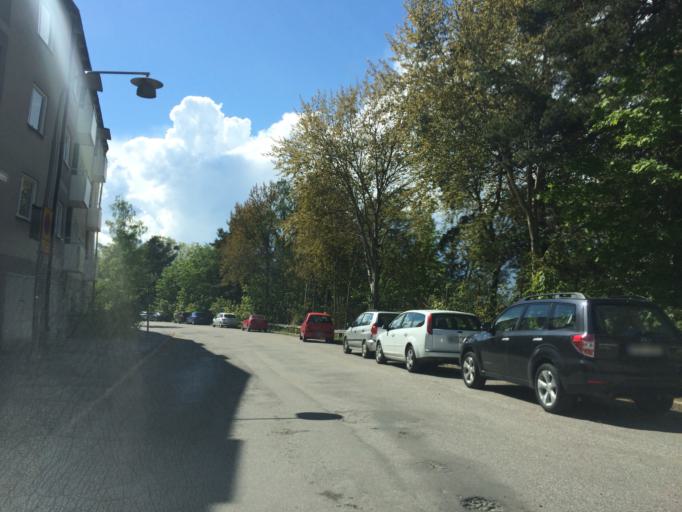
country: SE
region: Stockholm
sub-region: Huddinge Kommun
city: Segeltorp
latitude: 59.2875
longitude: 17.9583
